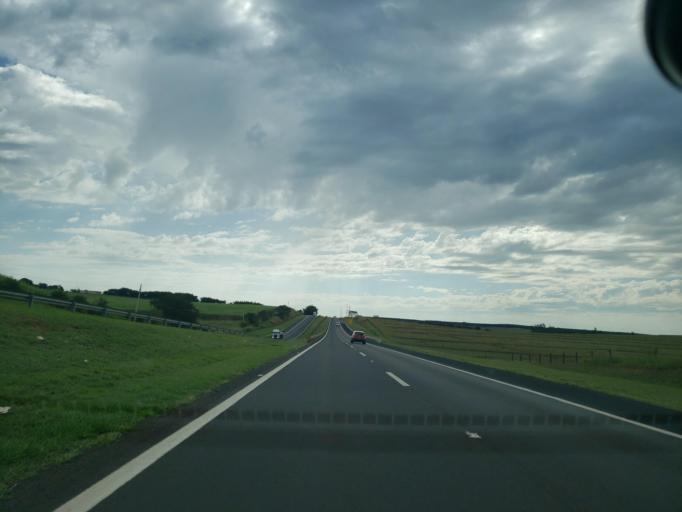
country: BR
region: Sao Paulo
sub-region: Cafelandia
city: Cafelandia
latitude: -21.7794
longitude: -49.6594
